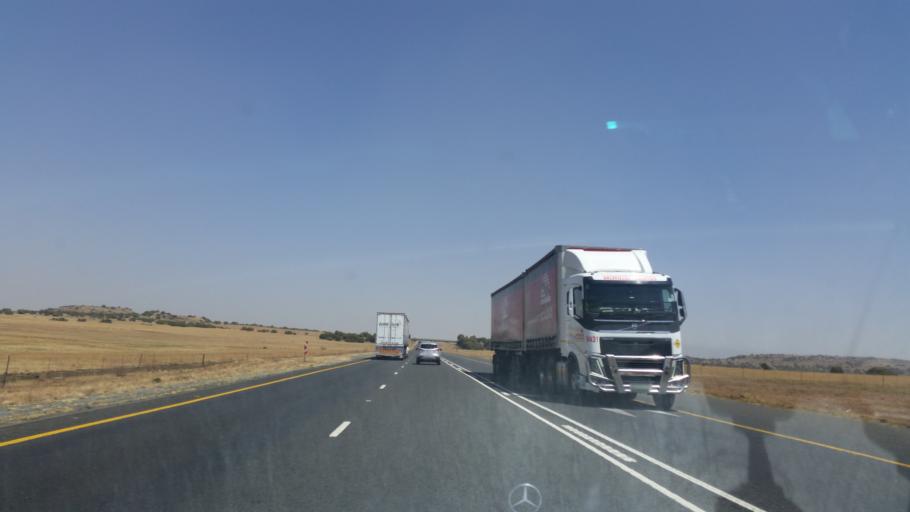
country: ZA
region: Orange Free State
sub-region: Lejweleputswa District Municipality
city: Winburg
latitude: -28.6930
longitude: 26.8107
